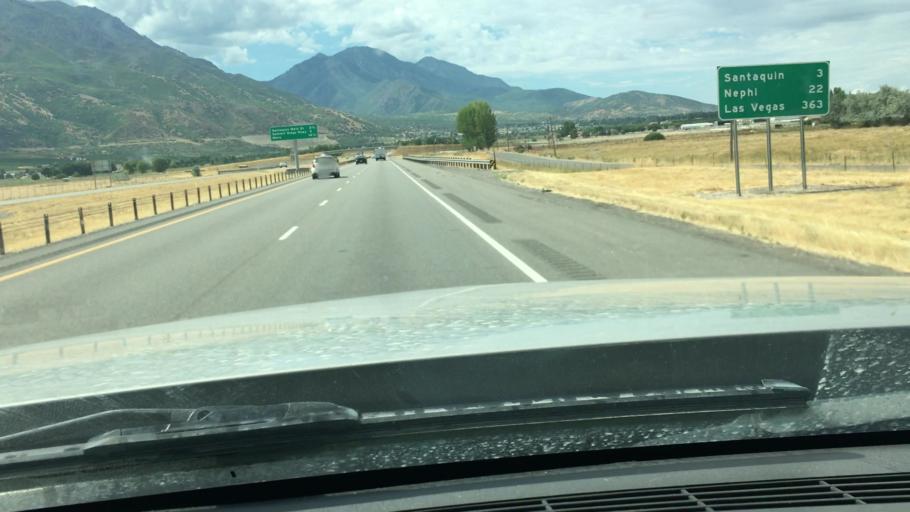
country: US
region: Utah
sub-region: Utah County
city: Payson
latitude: 40.0185
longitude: -111.7628
